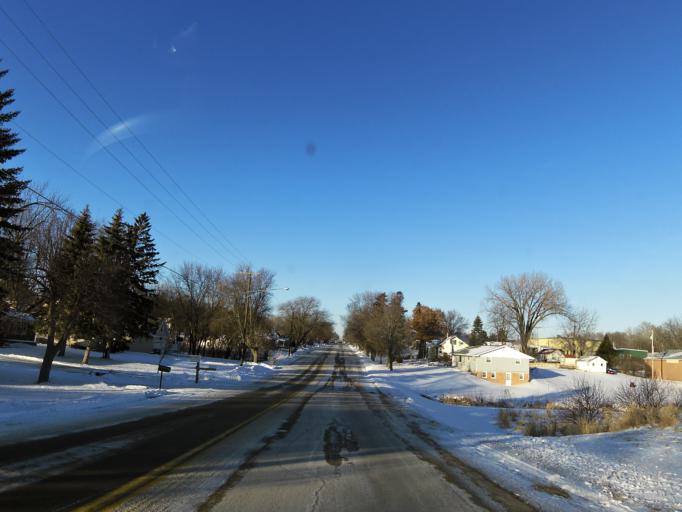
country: US
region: Minnesota
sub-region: Rice County
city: Lonsdale
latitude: 44.4749
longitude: -93.4285
